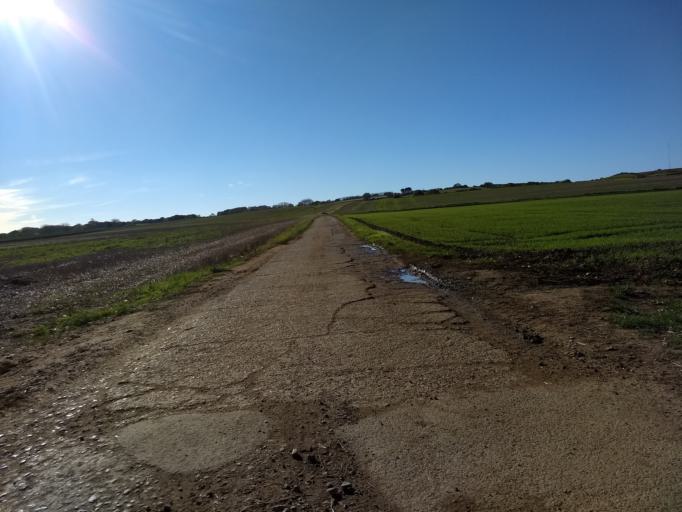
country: GB
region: England
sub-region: Isle of Wight
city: Newport
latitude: 50.6638
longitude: -1.2651
